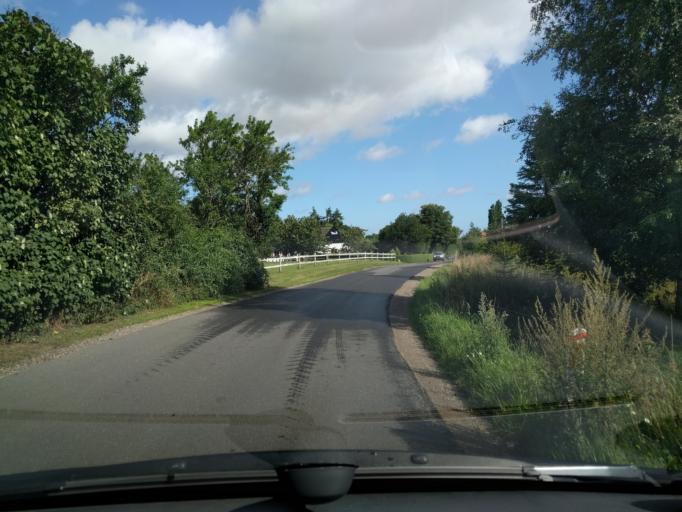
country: DK
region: South Denmark
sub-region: Kerteminde Kommune
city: Langeskov
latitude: 55.3670
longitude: 10.5872
